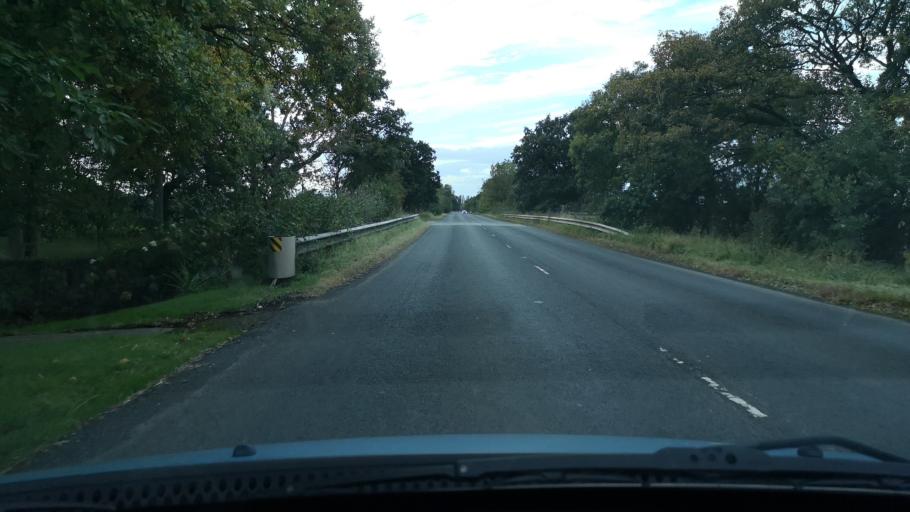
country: GB
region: England
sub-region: Doncaster
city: Hatfield
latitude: 53.5958
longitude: -0.9639
